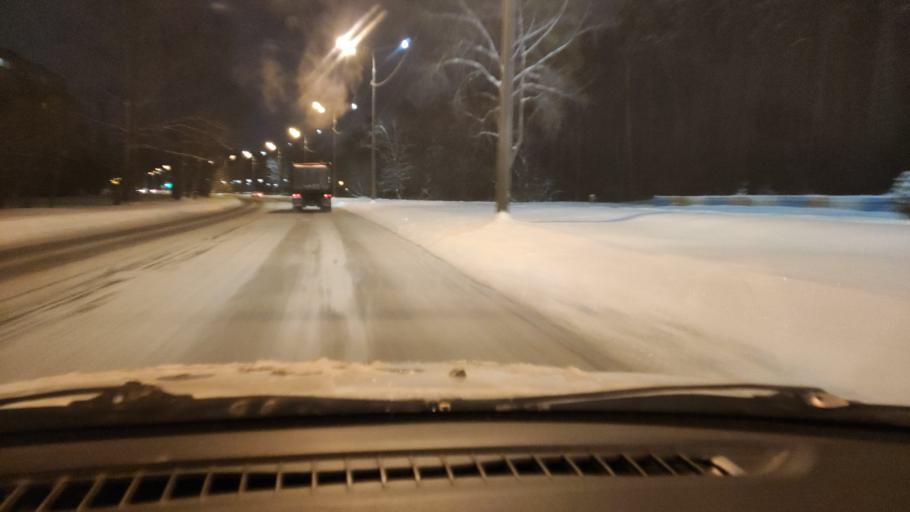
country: RU
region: Perm
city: Kondratovo
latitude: 57.9923
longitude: 56.1494
